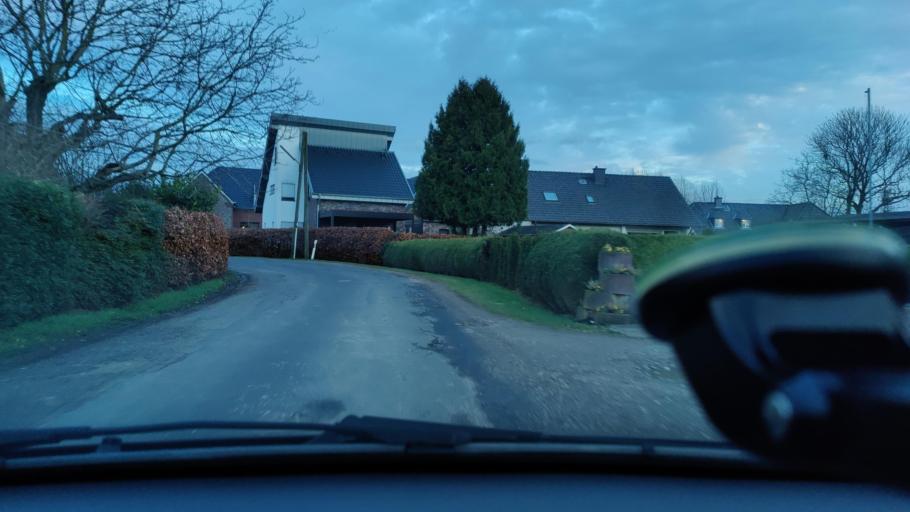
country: DE
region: North Rhine-Westphalia
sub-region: Regierungsbezirk Dusseldorf
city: Xanten
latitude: 51.6857
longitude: 6.4295
